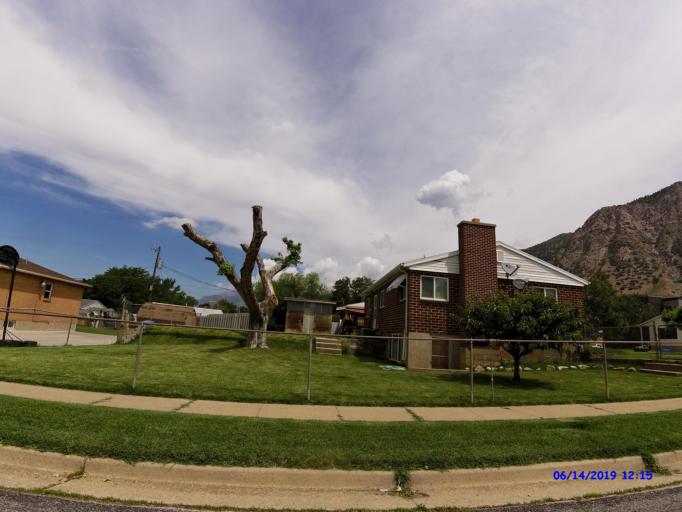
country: US
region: Utah
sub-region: Weber County
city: Ogden
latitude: 41.2575
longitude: -111.9510
